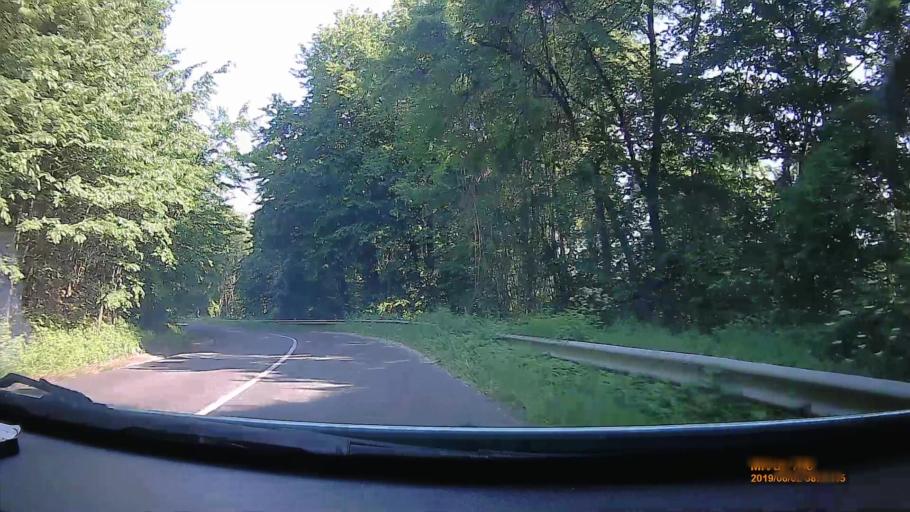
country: HU
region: Borsod-Abauj-Zemplen
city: Sajobabony
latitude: 48.1526
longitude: 20.6687
